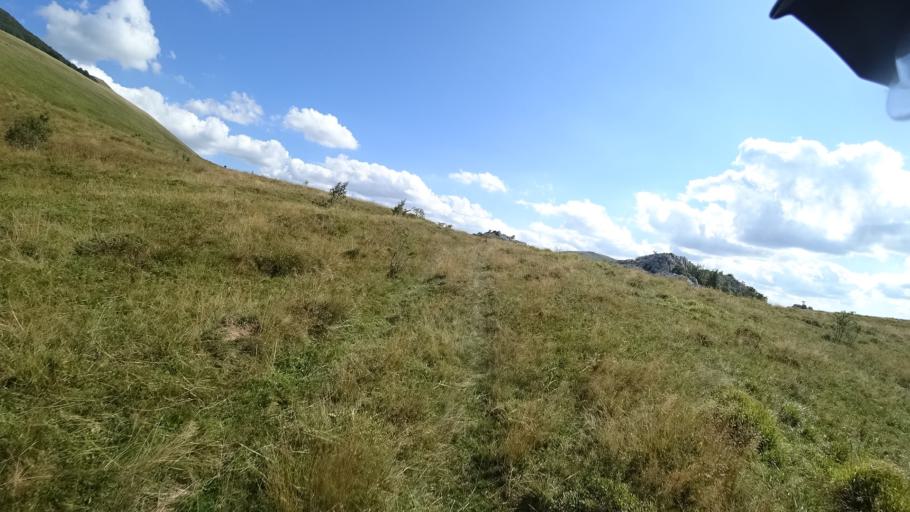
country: HR
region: Zadarska
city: Gracac
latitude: 44.4098
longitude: 16.0018
